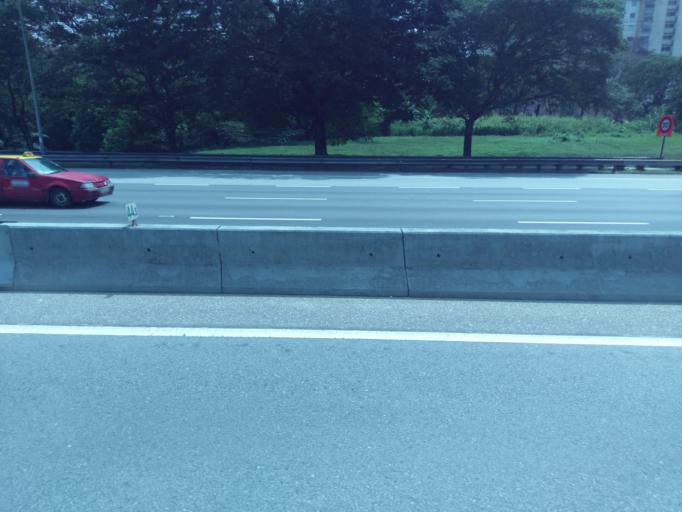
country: MY
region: Selangor
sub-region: Petaling
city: Petaling Jaya
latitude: 3.0690
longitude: 101.6386
